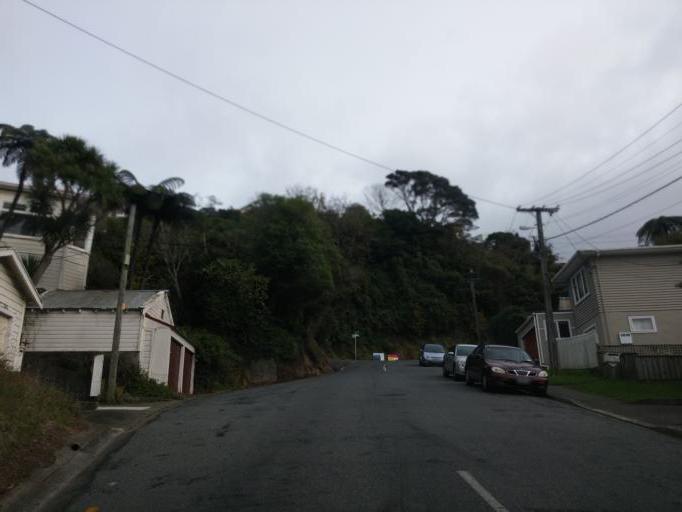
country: NZ
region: Wellington
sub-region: Wellington City
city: Brooklyn
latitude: -41.3130
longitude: 174.7675
